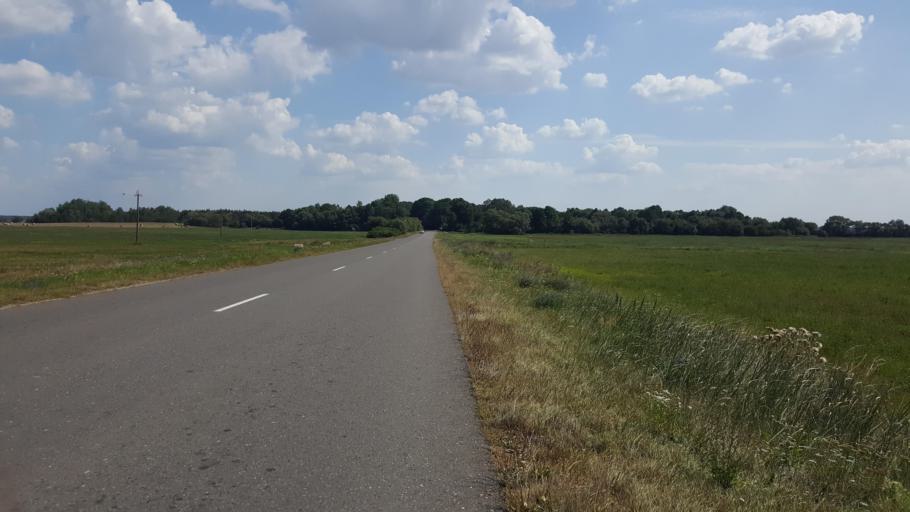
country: BY
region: Brest
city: Kamyanyuki
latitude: 52.4943
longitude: 23.6784
